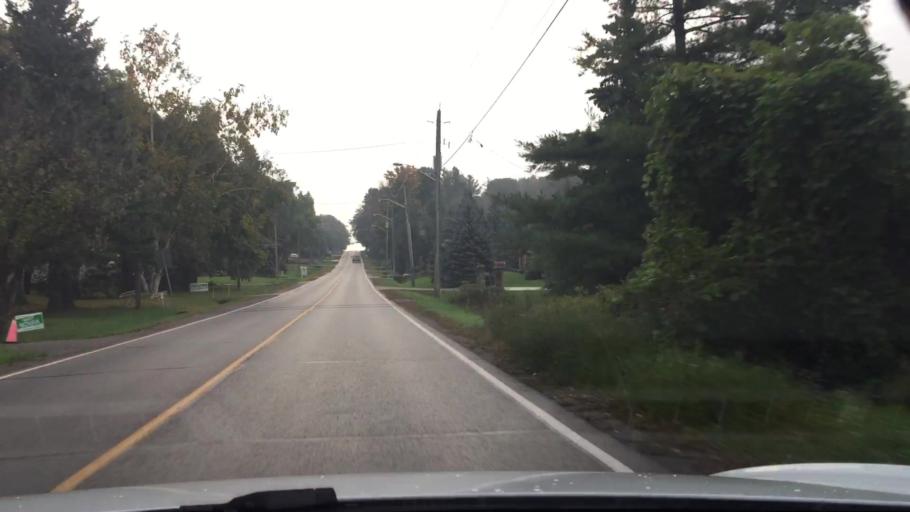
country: CA
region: Ontario
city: Oshawa
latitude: 43.9438
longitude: -78.8030
